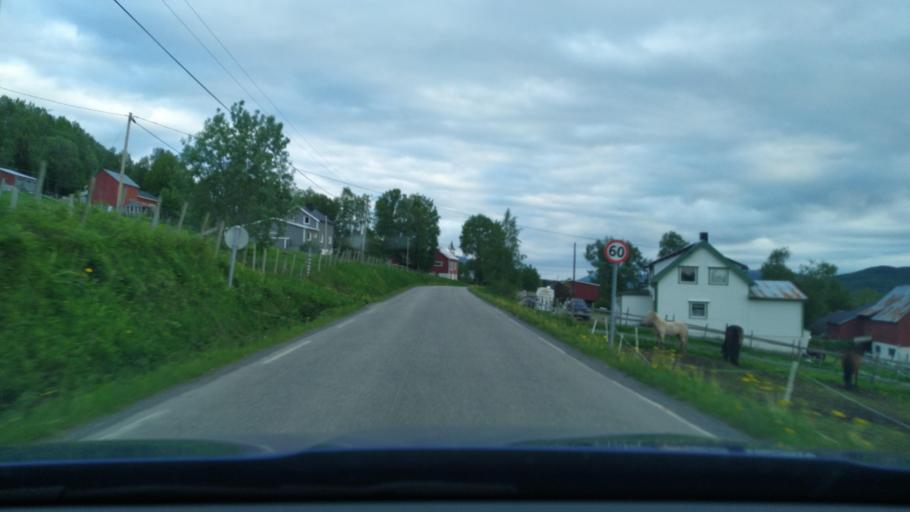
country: NO
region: Troms
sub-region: Tranoy
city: Vangsvika
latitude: 69.1146
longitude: 17.7948
